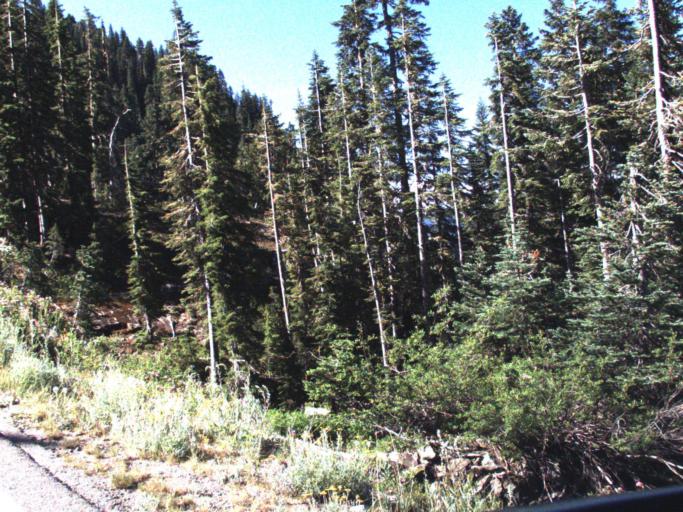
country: US
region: Washington
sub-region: King County
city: Enumclaw
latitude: 46.8666
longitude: -121.5246
